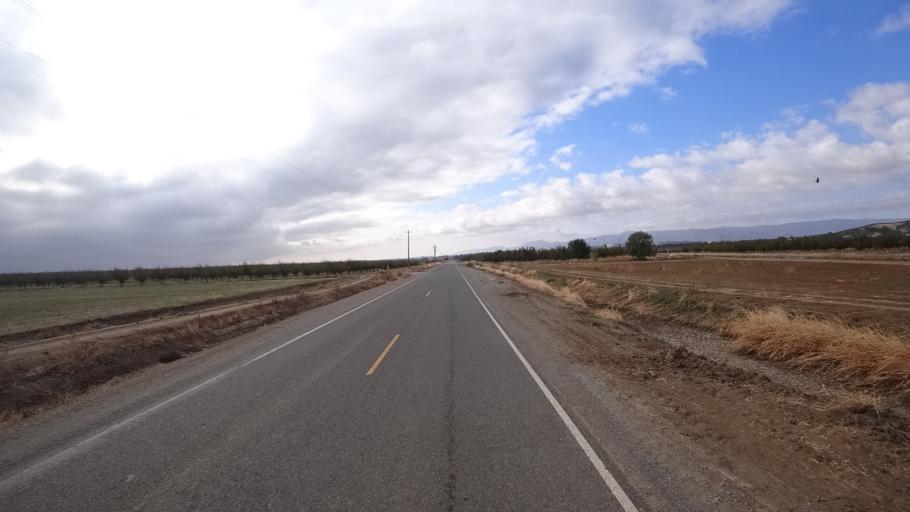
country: US
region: California
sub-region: Yolo County
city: Esparto
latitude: 38.7342
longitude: -122.0454
